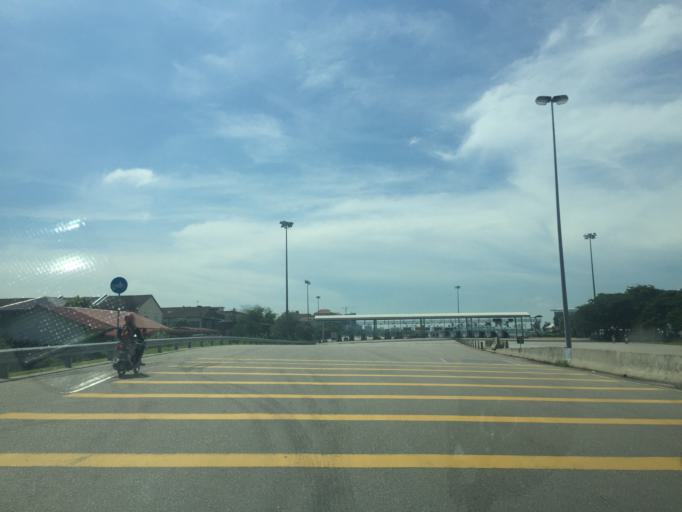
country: MY
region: Penang
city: Permatang Kuching
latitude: 5.4336
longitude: 100.3777
